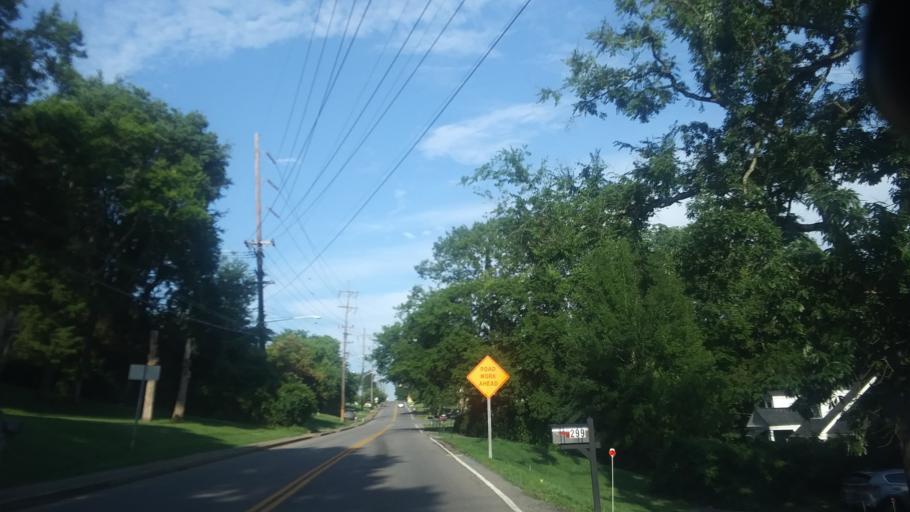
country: US
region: Tennessee
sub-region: Davidson County
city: Oak Hill
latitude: 36.0794
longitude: -86.7128
